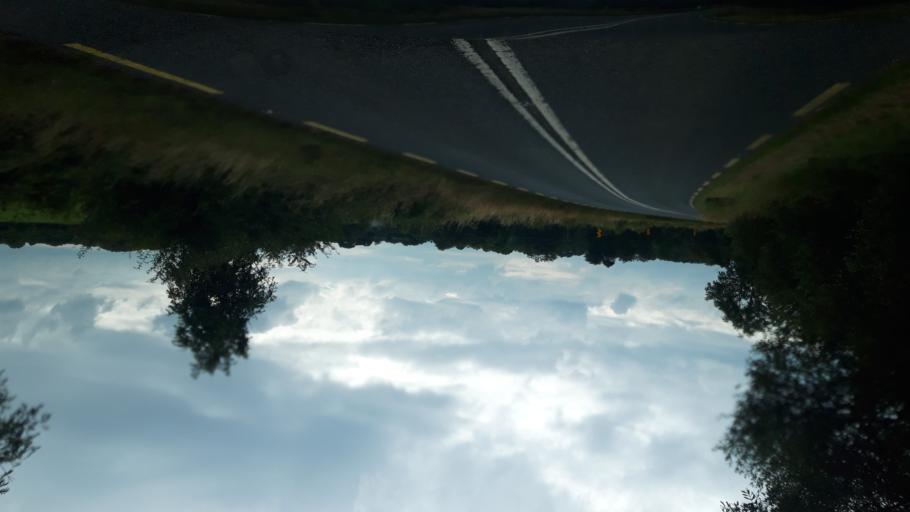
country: IE
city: Ballylinan
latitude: 52.8816
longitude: -7.0847
